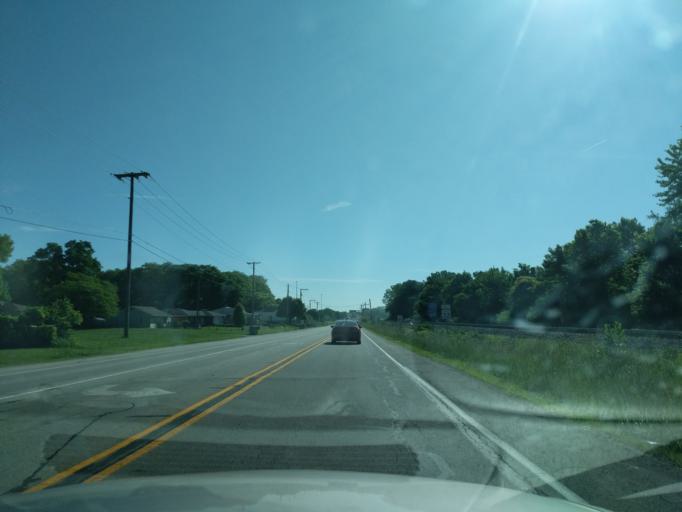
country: US
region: Indiana
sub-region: Delaware County
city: Daleville
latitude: 40.1156
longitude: -85.5758
